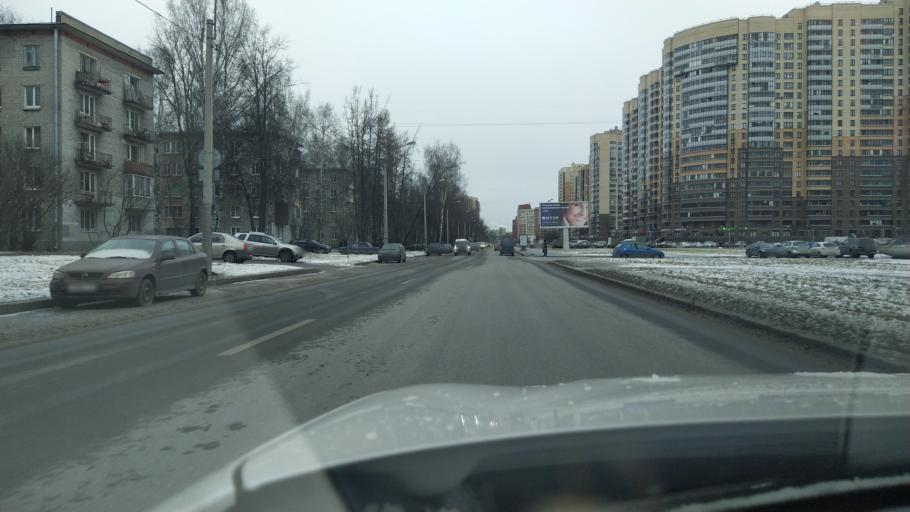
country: RU
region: Leningrad
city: Kalininskiy
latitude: 60.0014
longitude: 30.3962
